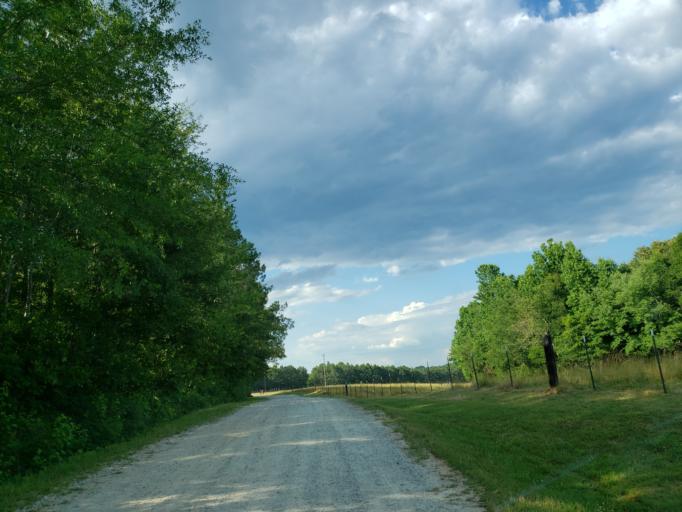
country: US
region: Georgia
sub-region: Haralson County
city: Buchanan
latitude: 33.8538
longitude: -85.2033
